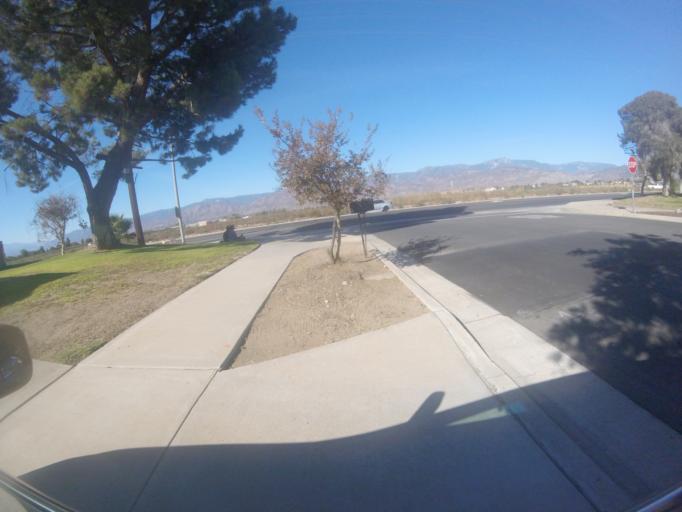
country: US
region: California
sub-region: San Bernardino County
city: Mentone
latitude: 34.0698
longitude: -117.1520
